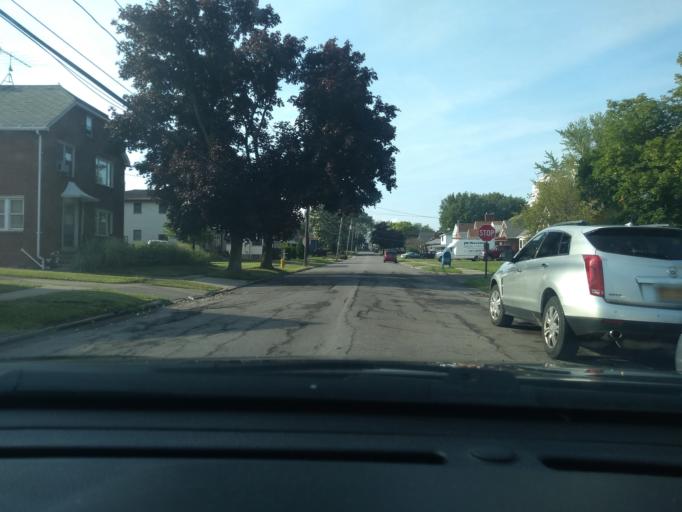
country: US
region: New York
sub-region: Erie County
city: Lackawanna
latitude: 42.8255
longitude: -78.8126
